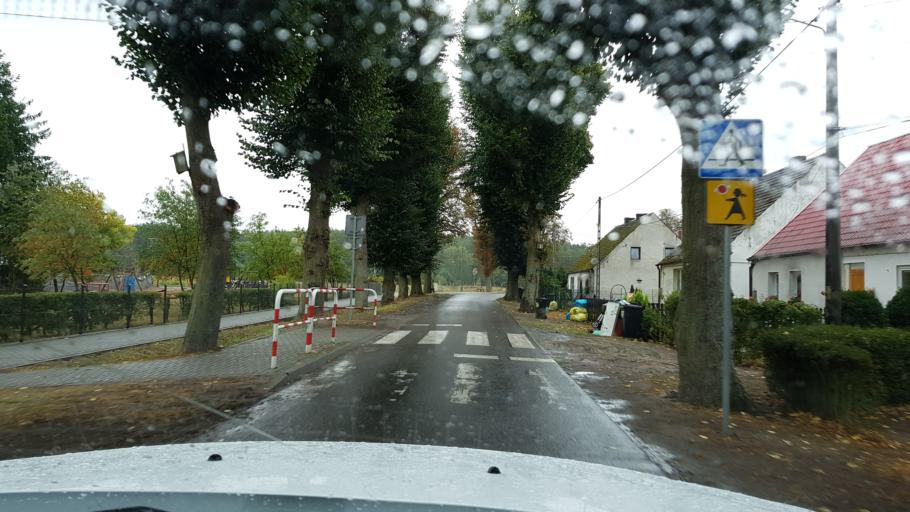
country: DE
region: Brandenburg
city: Schoneberg
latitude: 52.9757
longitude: 14.2077
